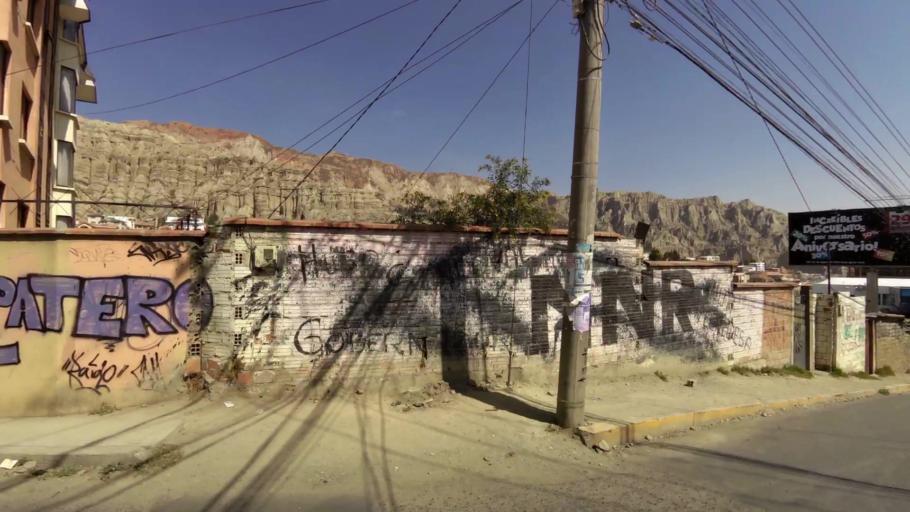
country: BO
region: La Paz
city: La Paz
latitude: -16.5452
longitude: -68.0690
